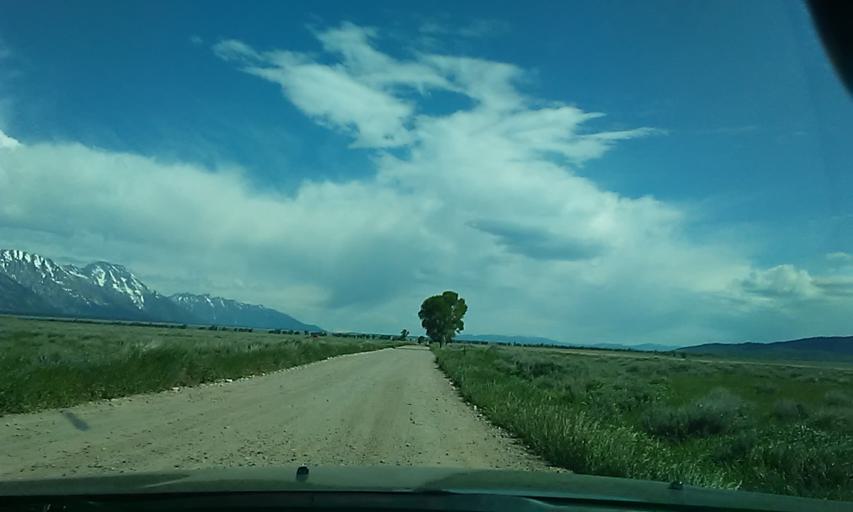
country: US
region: Wyoming
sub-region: Teton County
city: Jackson
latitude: 43.6283
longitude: -110.6641
